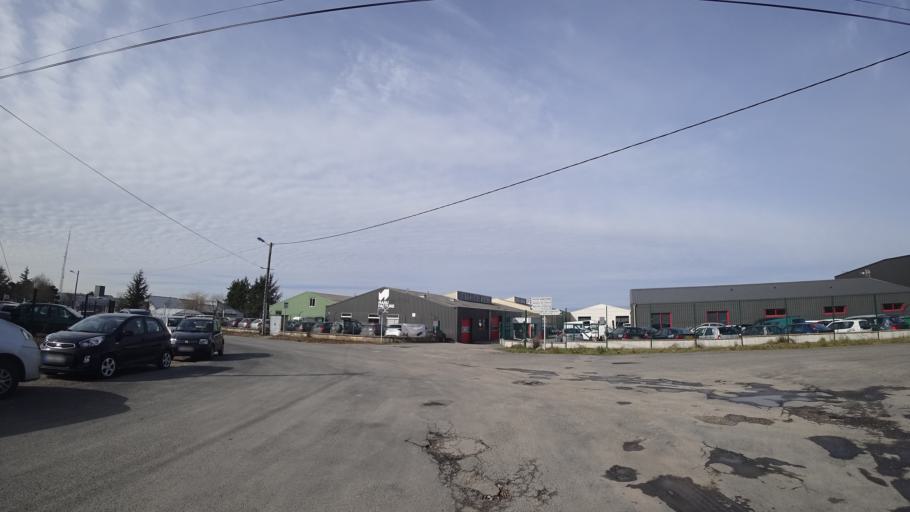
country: FR
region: Midi-Pyrenees
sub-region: Departement de l'Aveyron
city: Olemps
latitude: 44.3768
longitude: 2.5494
